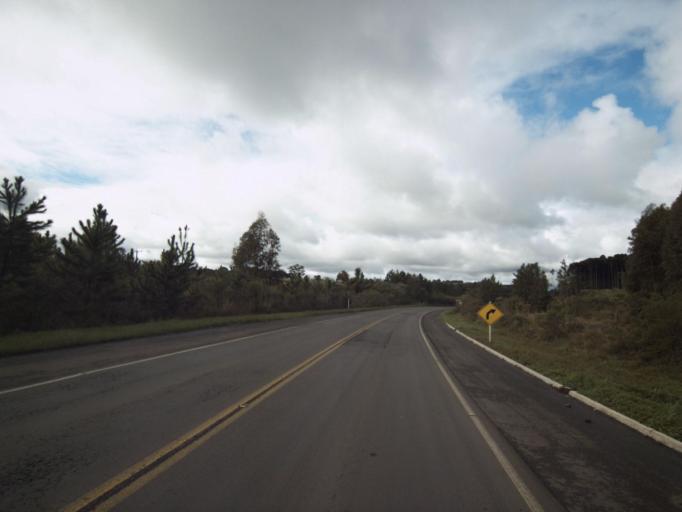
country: BR
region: Santa Catarina
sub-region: Concordia
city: Concordia
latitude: -27.2176
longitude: -51.9505
